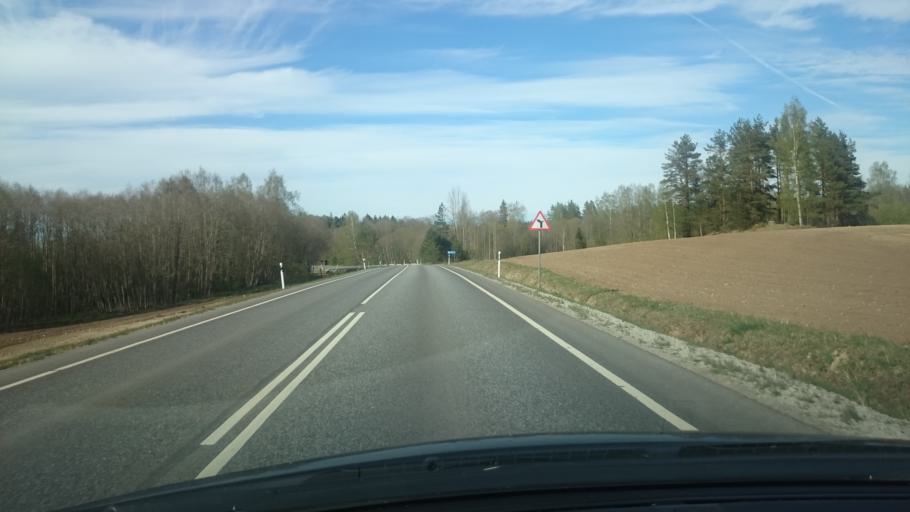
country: EE
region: Ida-Virumaa
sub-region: Johvi vald
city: Johvi
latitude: 59.2395
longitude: 27.5169
